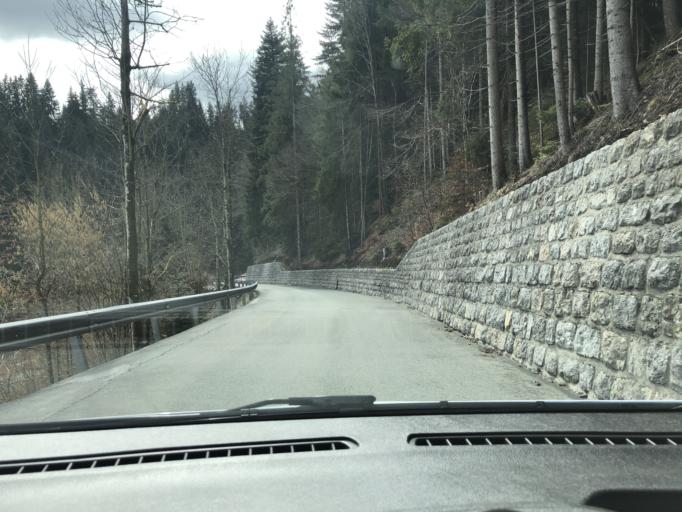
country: AT
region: Tyrol
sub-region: Politischer Bezirk Kitzbuhel
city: Hopfgarten im Brixental
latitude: 47.4476
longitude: 12.1508
